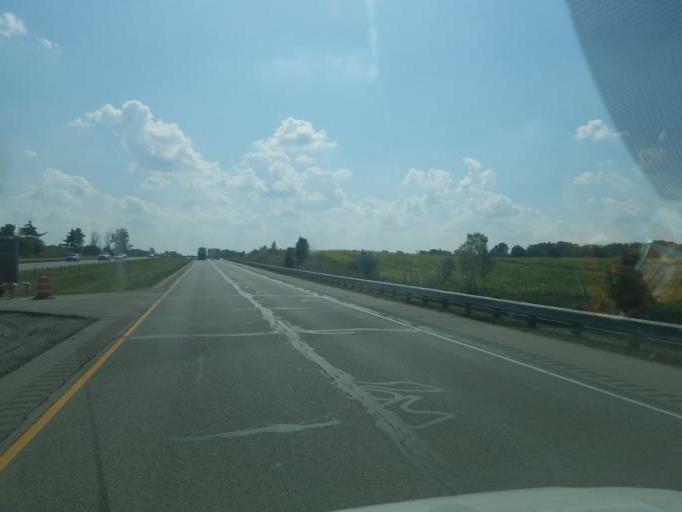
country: US
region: Indiana
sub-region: DeKalb County
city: Garrett
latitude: 41.2865
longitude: -85.0873
